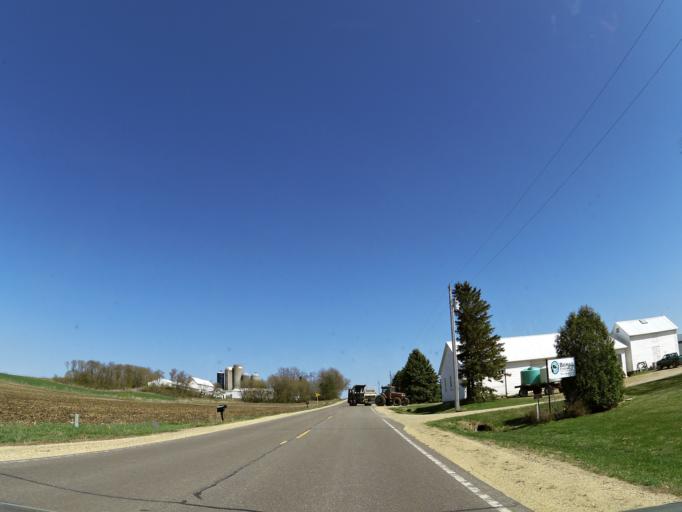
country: US
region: Wisconsin
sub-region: Saint Croix County
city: Hammond
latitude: 44.9347
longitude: -92.4753
